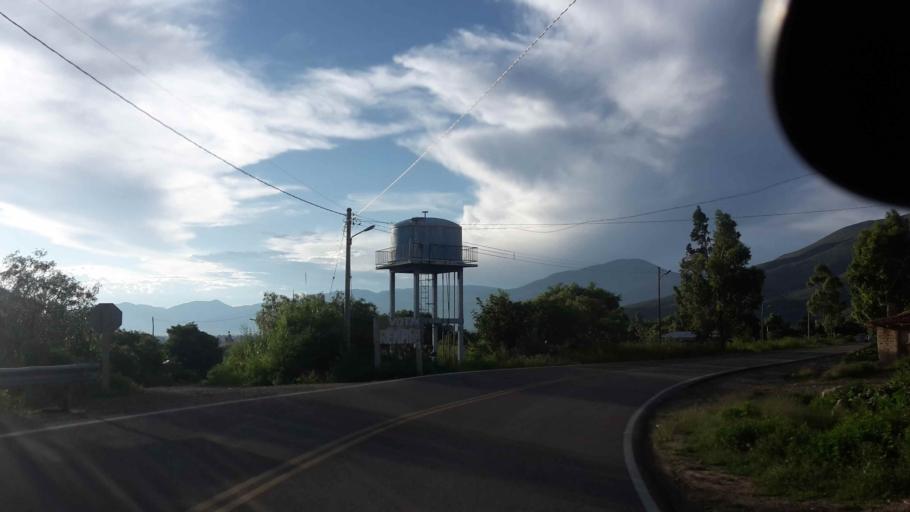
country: BO
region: Cochabamba
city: Arani
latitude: -17.5777
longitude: -65.7576
